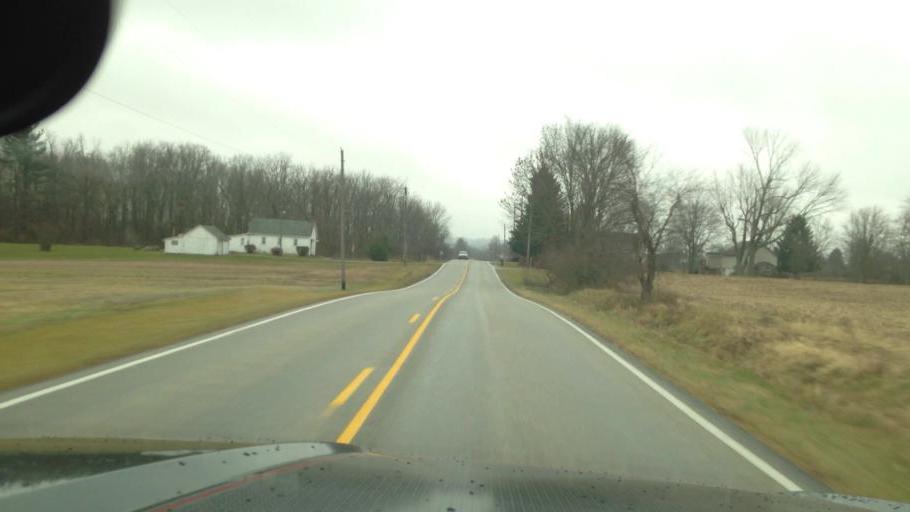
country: US
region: Ohio
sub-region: Preble County
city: New Paris
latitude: 39.9038
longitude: -84.8318
